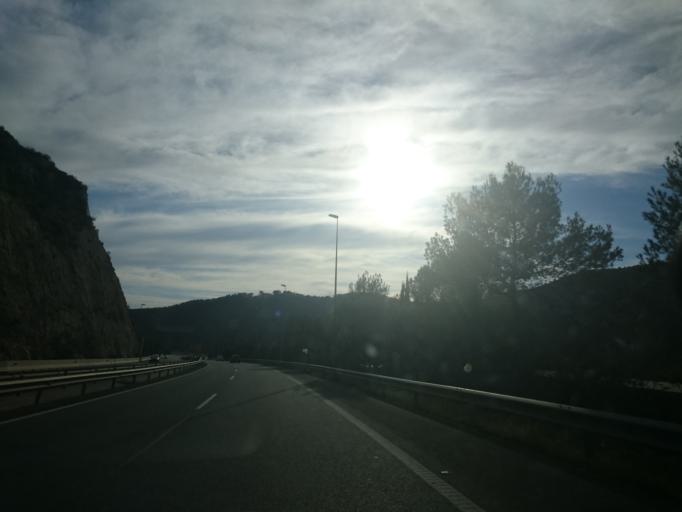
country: ES
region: Catalonia
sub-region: Provincia de Barcelona
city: Sitges
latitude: 41.2478
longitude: 1.8633
